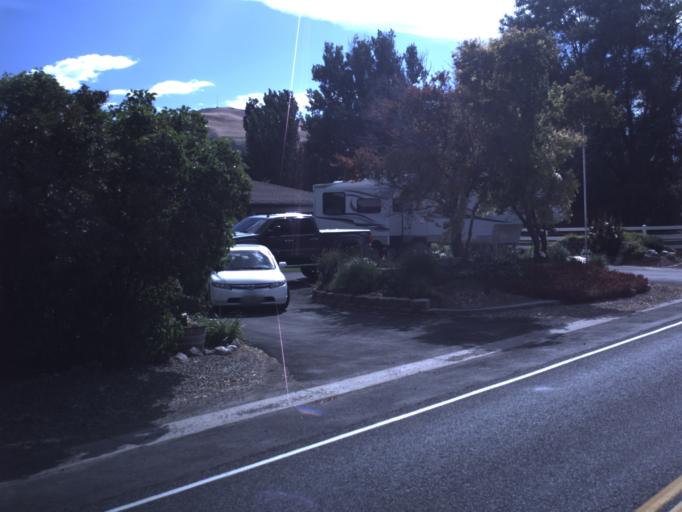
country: US
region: Utah
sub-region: Cache County
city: Lewiston
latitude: 41.9176
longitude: -111.9369
